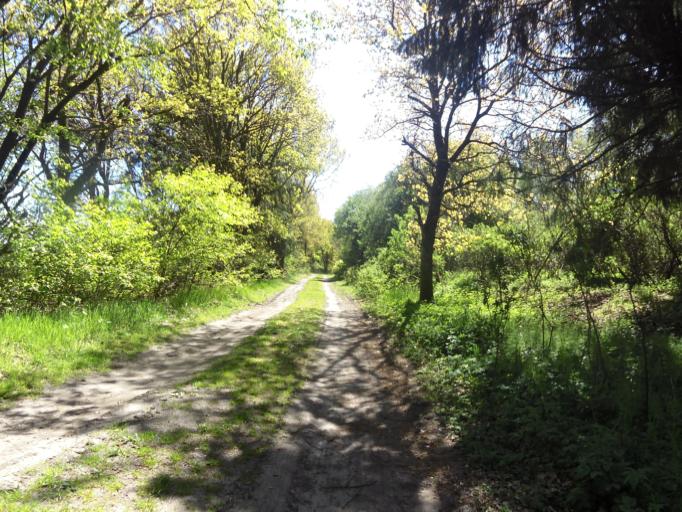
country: DK
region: South Denmark
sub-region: Tonder Kommune
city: Sherrebek
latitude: 55.2332
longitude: 8.7325
